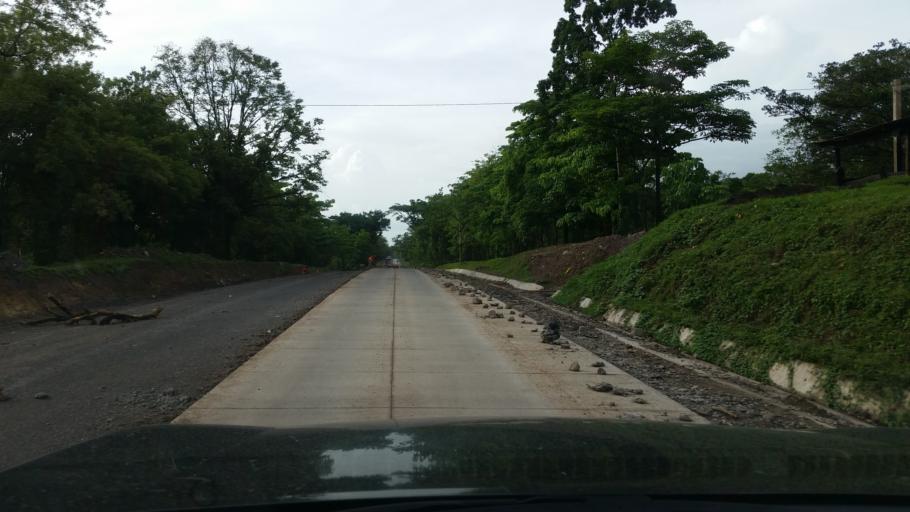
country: NI
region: Matagalpa
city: Rio Blanco
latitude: 13.0857
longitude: -85.0620
